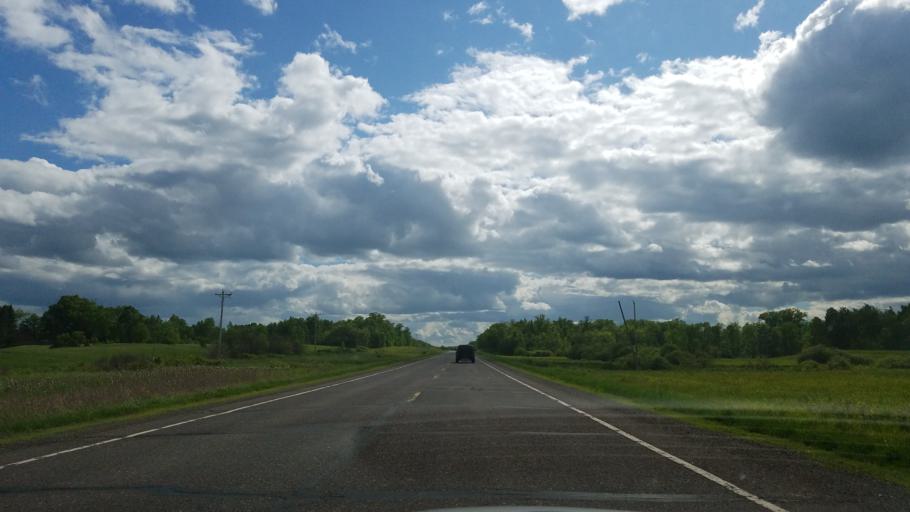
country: US
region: Wisconsin
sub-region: Burnett County
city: Siren
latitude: 46.1850
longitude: -92.1921
